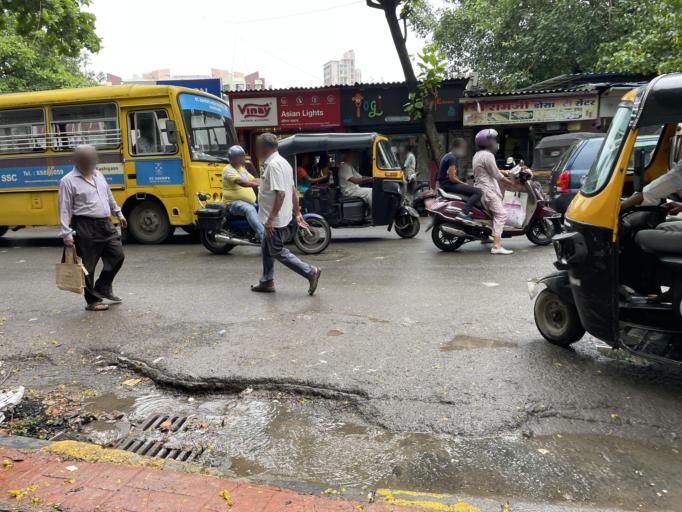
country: IN
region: Maharashtra
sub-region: Mumbai Suburban
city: Borivli
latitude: 19.2526
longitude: 72.8630
